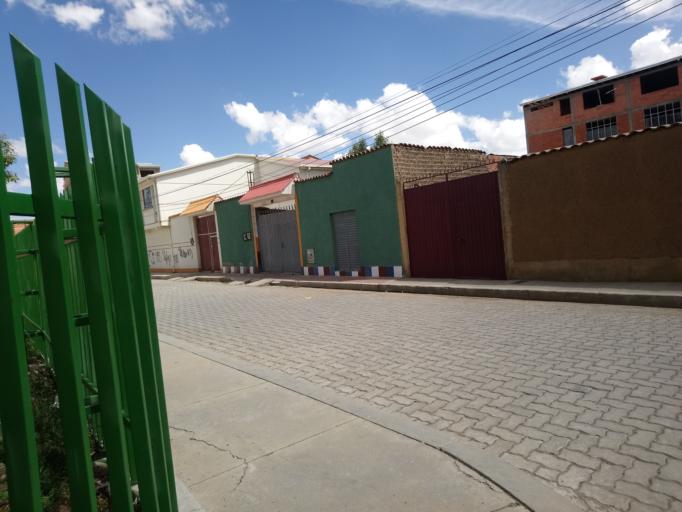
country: BO
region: La Paz
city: La Paz
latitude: -16.5565
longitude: -68.1920
